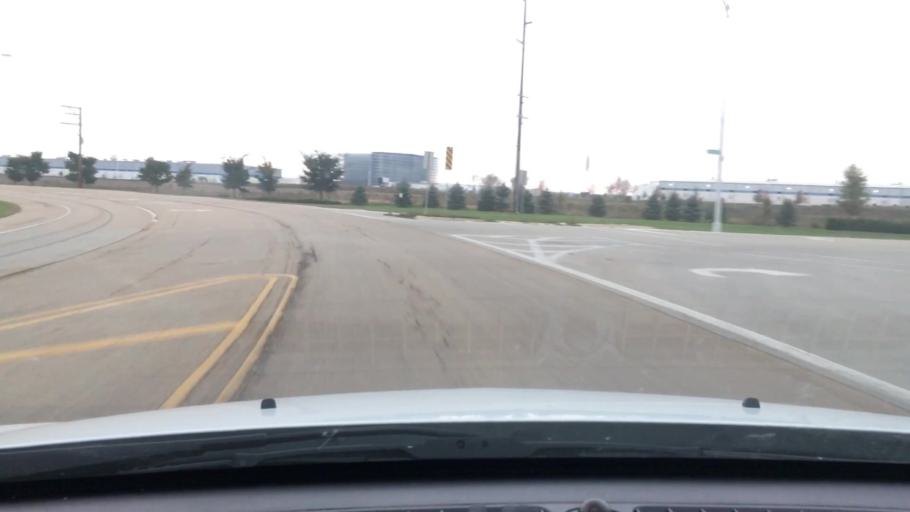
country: US
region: Illinois
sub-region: Ogle County
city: Rochelle
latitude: 41.8975
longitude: -89.0293
